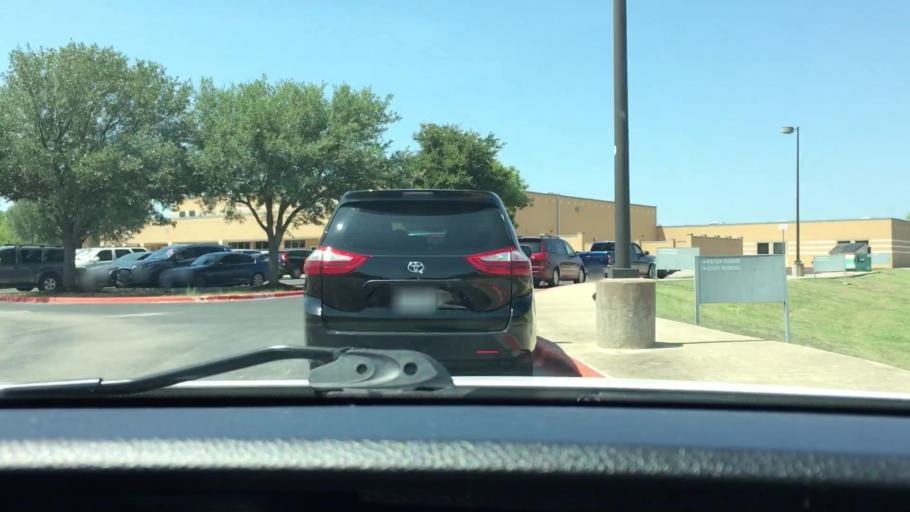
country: US
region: Texas
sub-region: Travis County
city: Windemere
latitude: 30.4676
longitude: -97.6546
